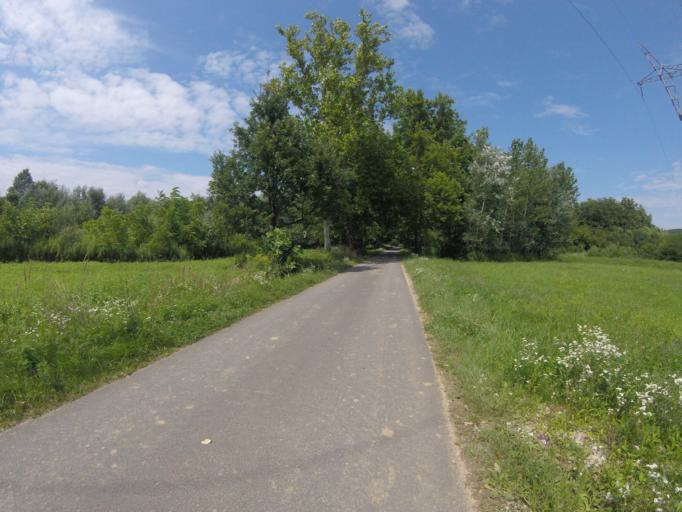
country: HR
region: Medimurska
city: Podturen
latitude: 46.5455
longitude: 16.6096
